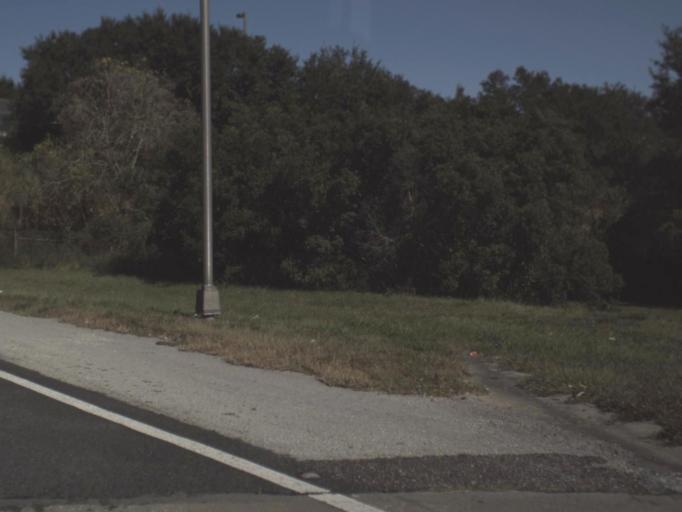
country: US
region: Florida
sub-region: Seminole County
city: Oviedo
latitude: 28.6617
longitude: -81.2297
